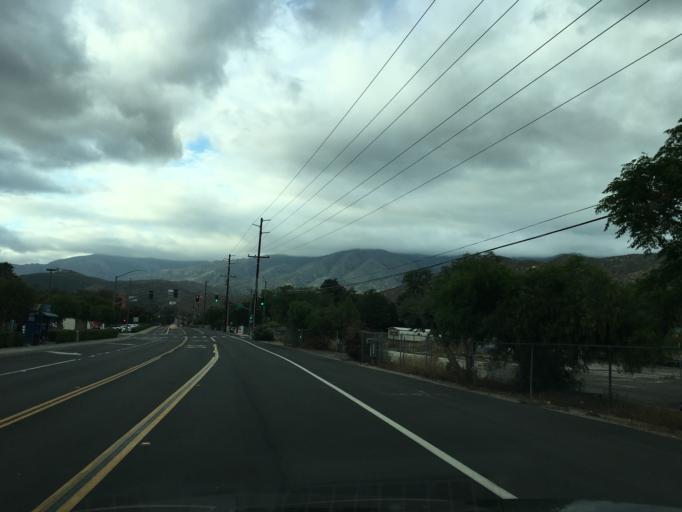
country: US
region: California
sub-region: San Diego County
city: Valley Center
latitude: 33.2649
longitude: -116.9539
